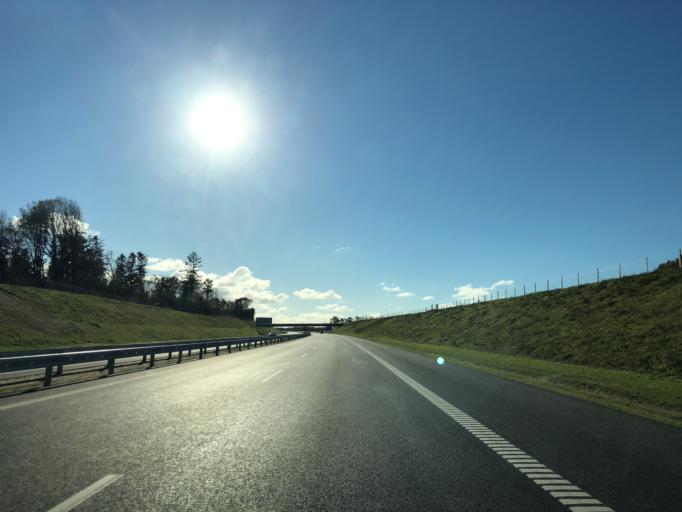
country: DK
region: Central Jutland
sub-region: Herning Kommune
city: Avlum
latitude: 56.3086
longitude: 8.7269
